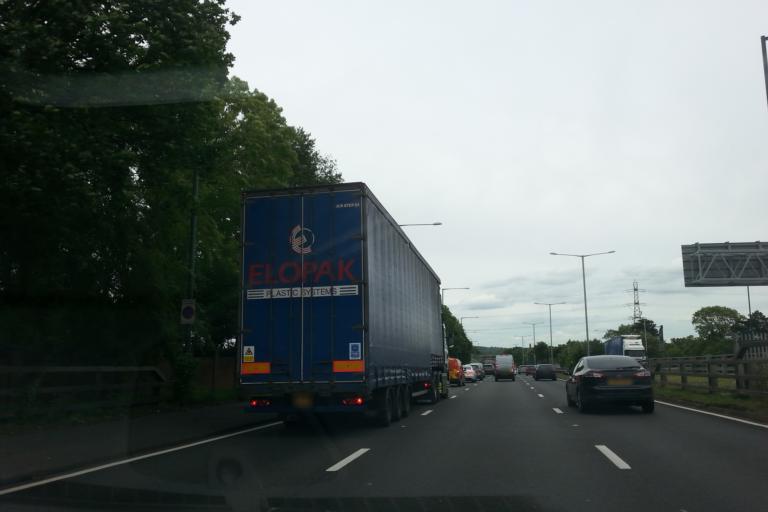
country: GB
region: England
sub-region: Solihull
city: Bickenhill
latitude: 52.4448
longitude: -1.7179
